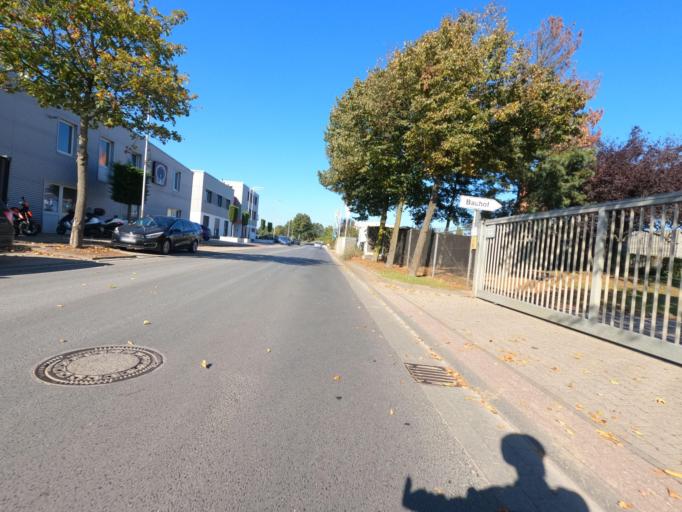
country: DE
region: North Rhine-Westphalia
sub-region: Regierungsbezirk Koln
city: Linnich
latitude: 50.9827
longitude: 6.2838
